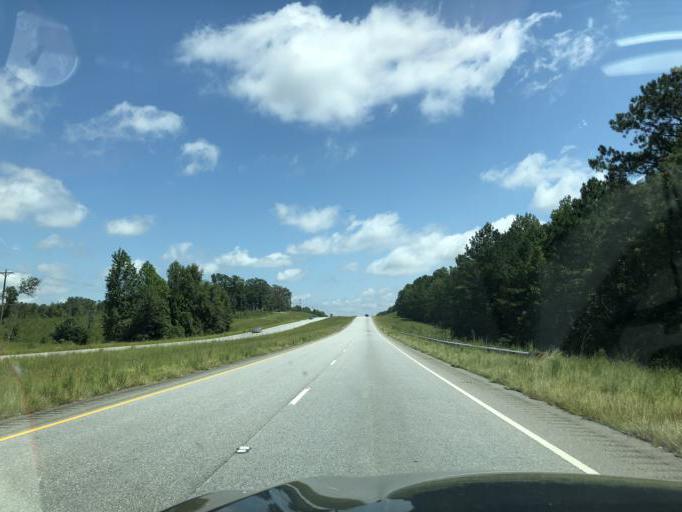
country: US
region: Alabama
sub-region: Barbour County
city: Eufaula
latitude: 31.7528
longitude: -85.2213
